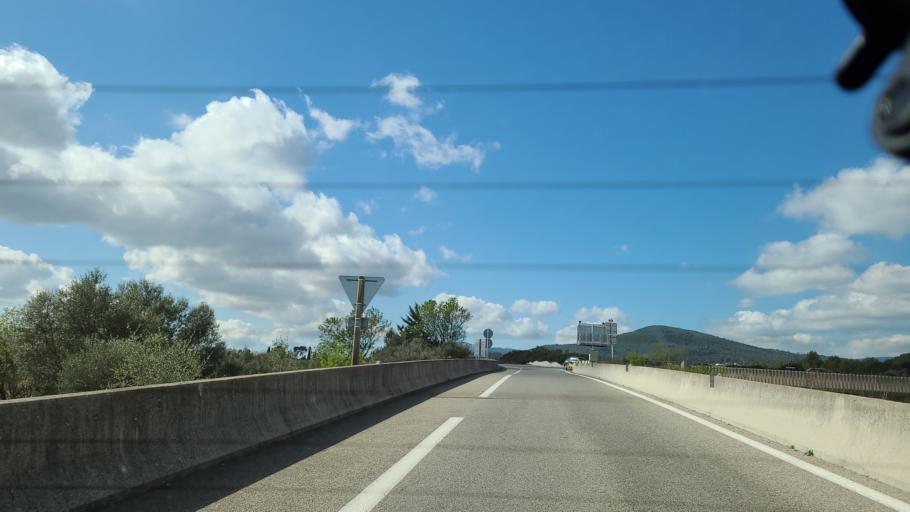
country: FR
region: Provence-Alpes-Cote d'Azur
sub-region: Departement du Var
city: Cuers
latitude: 43.2488
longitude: 6.0958
